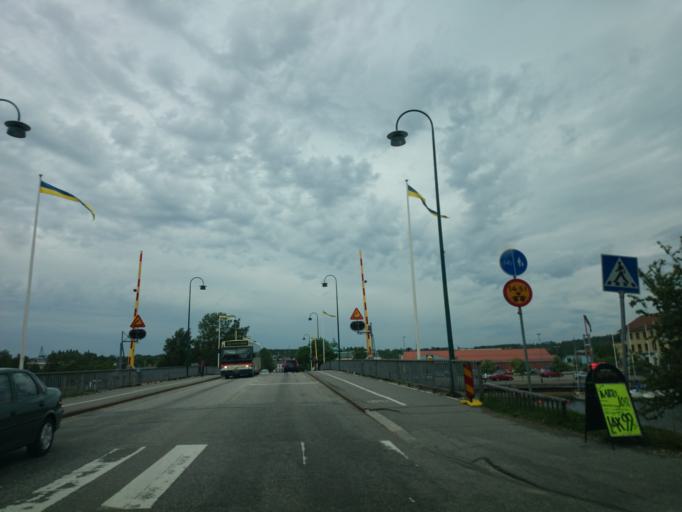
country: SE
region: Vaesternorrland
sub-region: Haernoesands Kommun
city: Haernoesand
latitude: 62.6336
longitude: 17.9377
